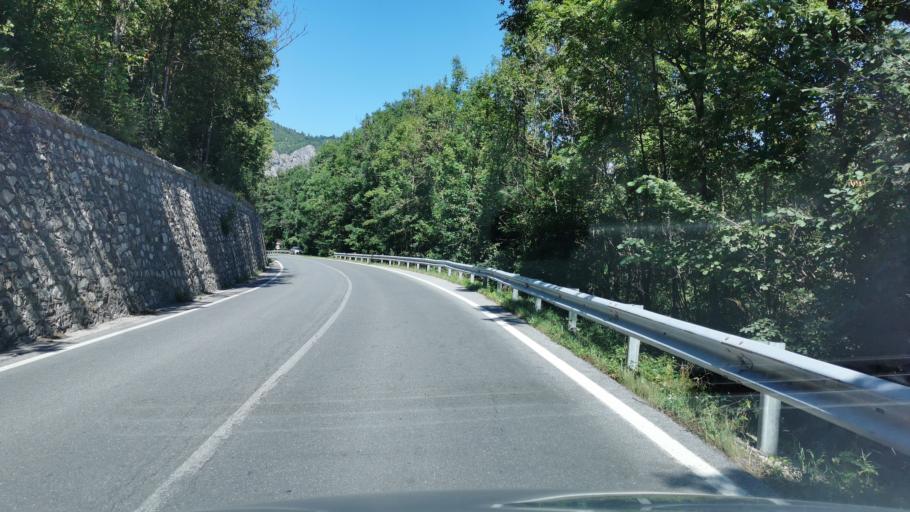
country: IT
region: Piedmont
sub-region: Provincia di Cuneo
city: Valdieri
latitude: 44.2881
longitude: 7.4201
